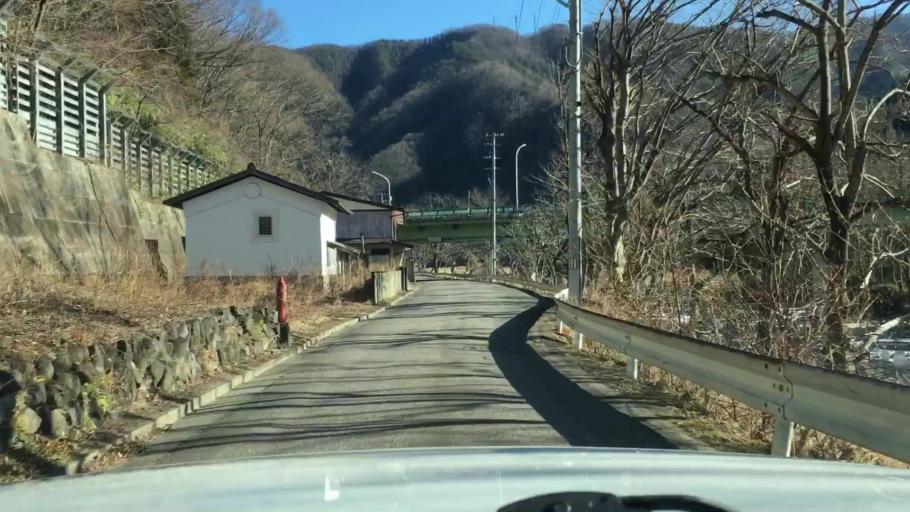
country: JP
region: Iwate
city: Miyako
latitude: 39.6211
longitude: 141.8023
